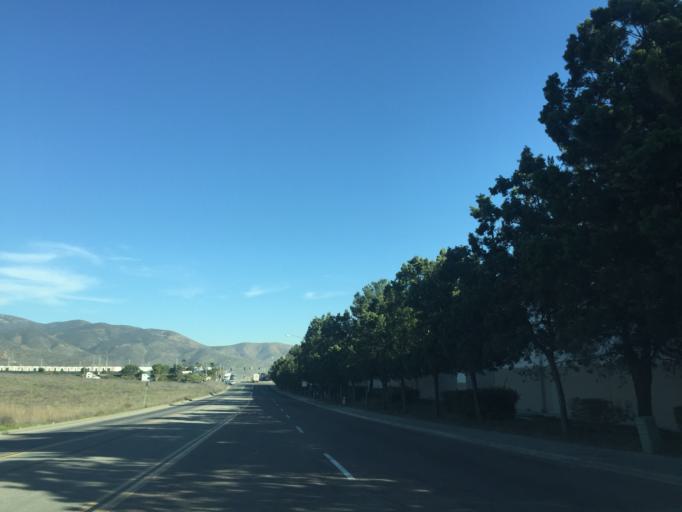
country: MX
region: Baja California
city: Tijuana
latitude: 32.5601
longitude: -116.9309
